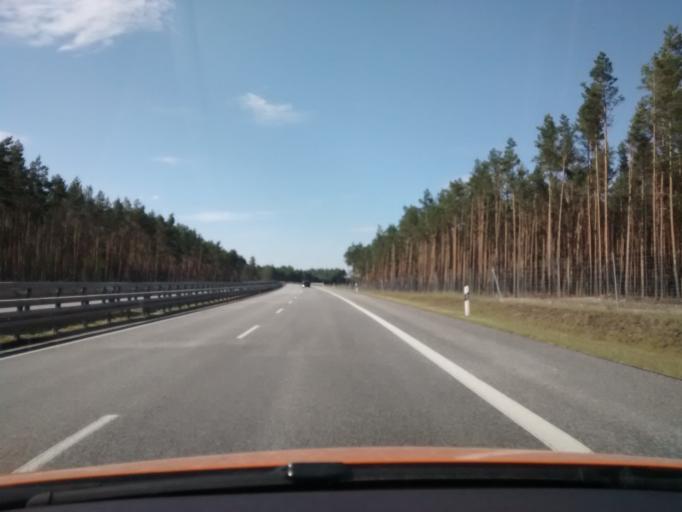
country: DE
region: Brandenburg
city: Trebbin
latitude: 52.1587
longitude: 13.2403
